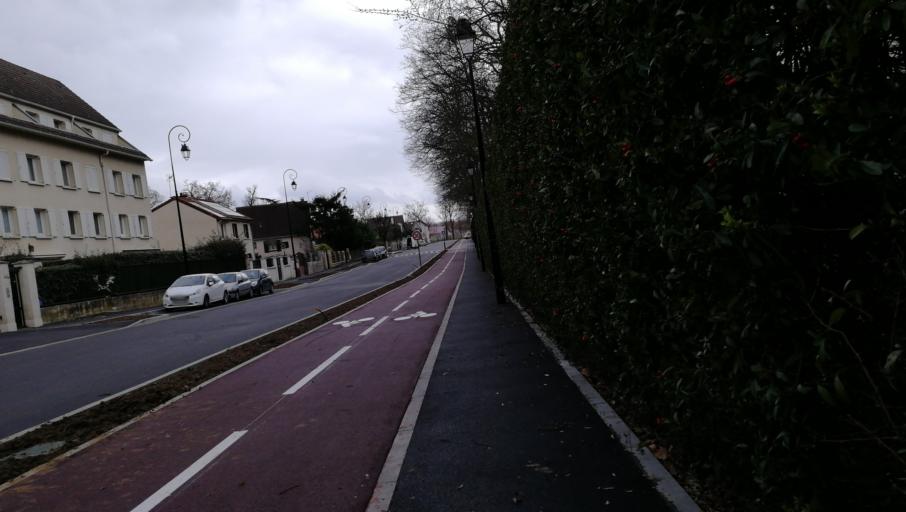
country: FR
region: Ile-de-France
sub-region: Departement du Val-de-Marne
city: Le Plessis-Trevise
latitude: 48.8052
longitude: 2.5783
